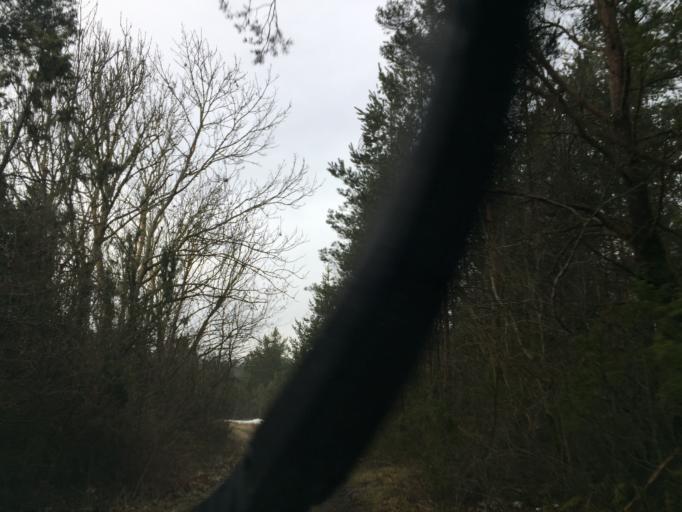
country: EE
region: Saare
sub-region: Orissaare vald
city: Orissaare
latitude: 58.6090
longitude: 22.9545
